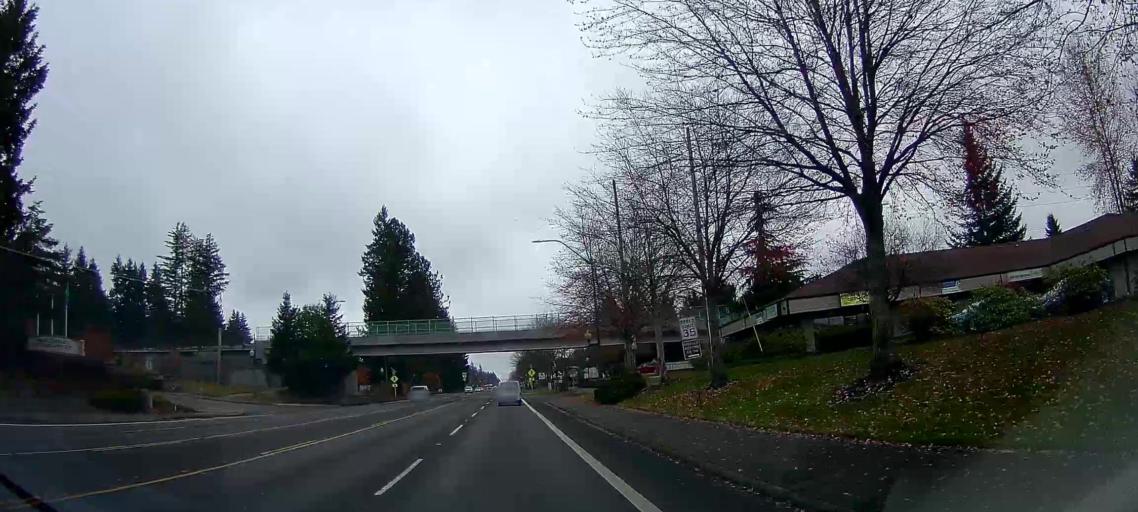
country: US
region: Washington
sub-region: Thurston County
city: Lacey
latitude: 47.0474
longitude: -122.8400
